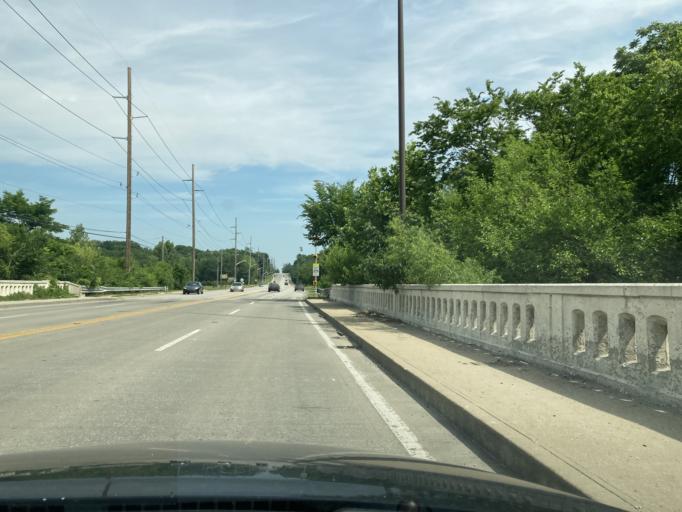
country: US
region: Indiana
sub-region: Marion County
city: Broad Ripple
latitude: 39.8326
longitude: -86.1845
